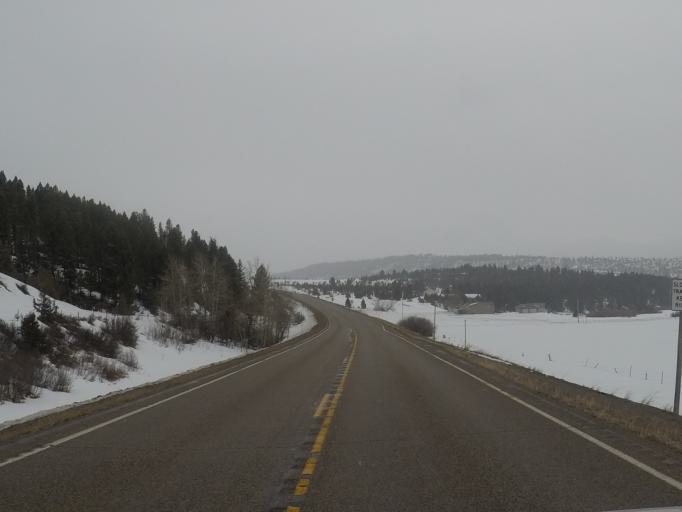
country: US
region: Montana
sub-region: Meagher County
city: White Sulphur Springs
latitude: 46.6713
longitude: -110.8778
